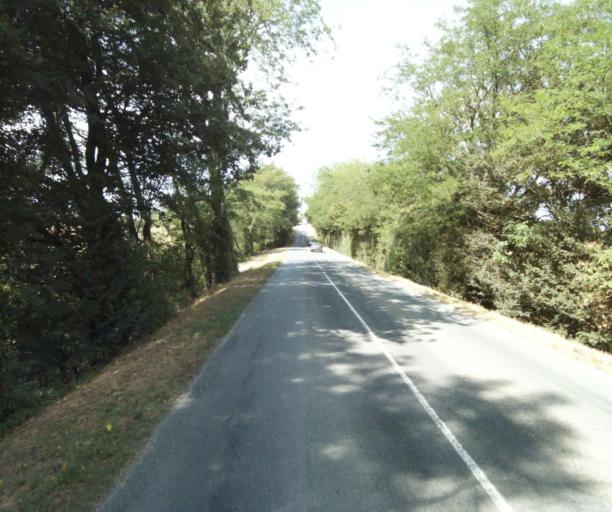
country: FR
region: Midi-Pyrenees
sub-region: Departement du Tarn
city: Puylaurens
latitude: 43.5228
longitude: 2.0090
